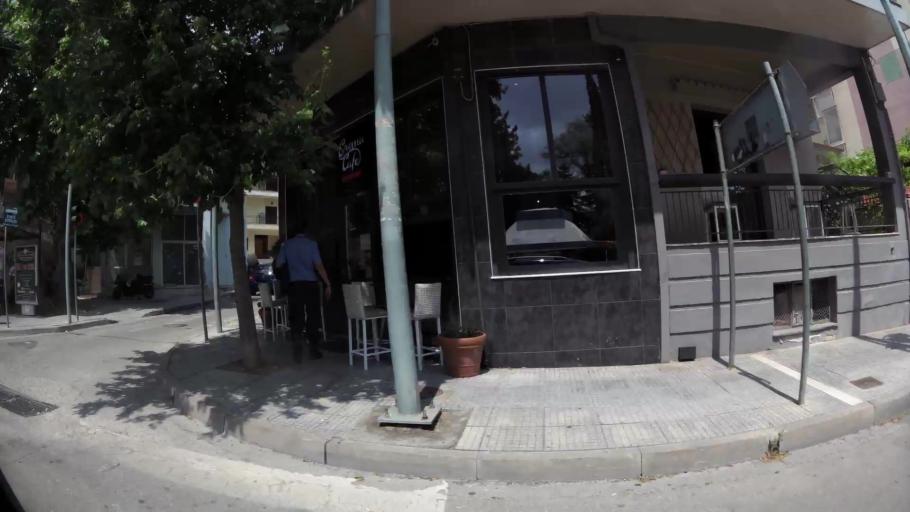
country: GR
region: West Macedonia
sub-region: Nomos Kozanis
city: Kozani
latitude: 40.3075
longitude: 21.7872
